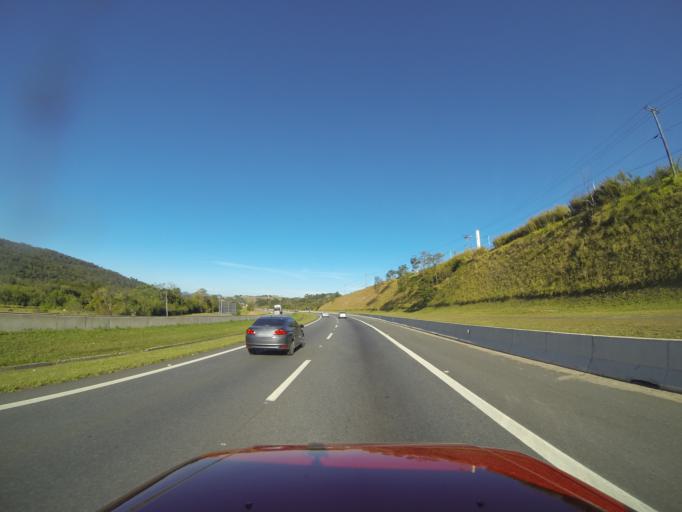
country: BR
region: Sao Paulo
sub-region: Bom Jesus Dos Perdoes
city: Bom Jesus dos Perdoes
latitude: -23.1693
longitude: -46.4420
